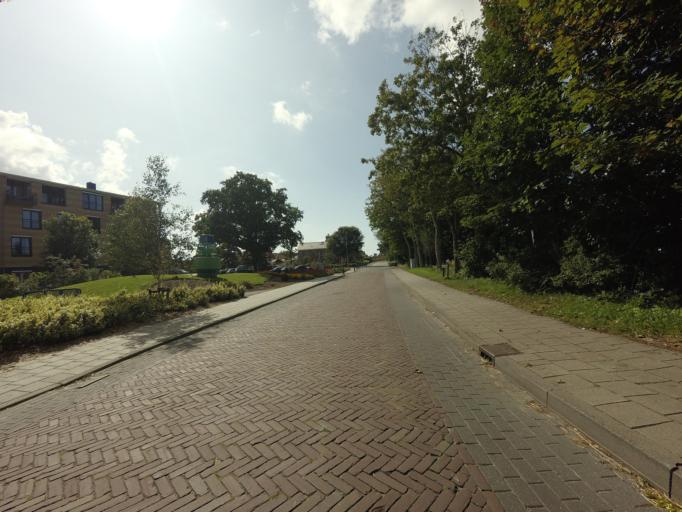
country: NL
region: Friesland
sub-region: Gemeente Terschelling
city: West-Terschelling
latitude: 53.3646
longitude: 5.2150
